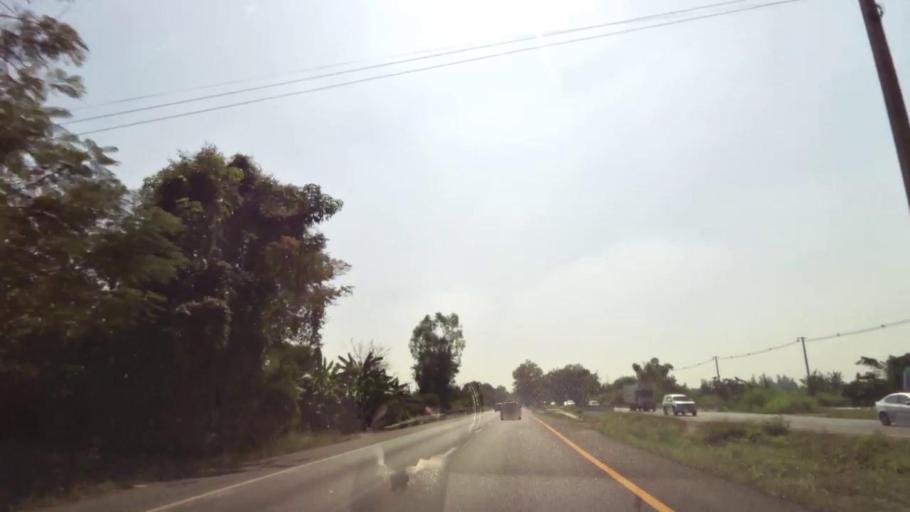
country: TH
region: Phichit
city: Bueng Na Rang
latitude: 16.0385
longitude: 100.1173
